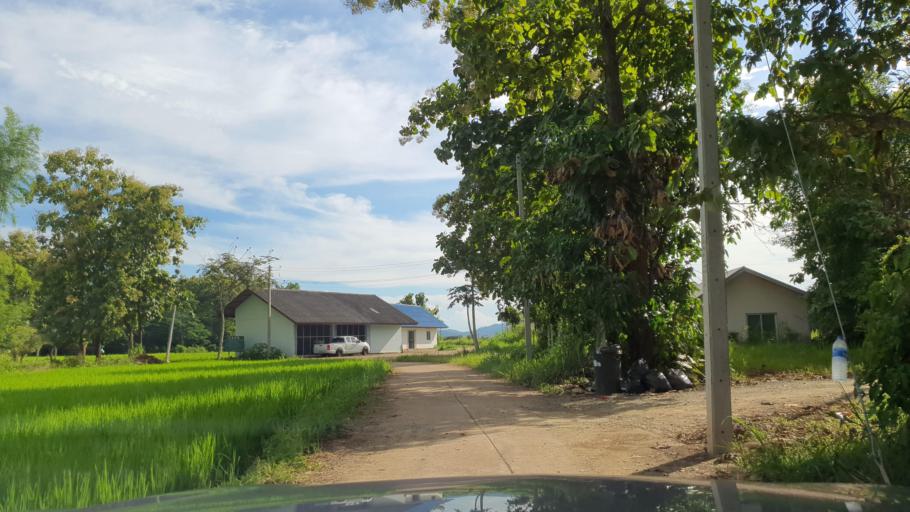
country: TH
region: Chiang Mai
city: Mae On
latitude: 18.7648
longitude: 99.2555
